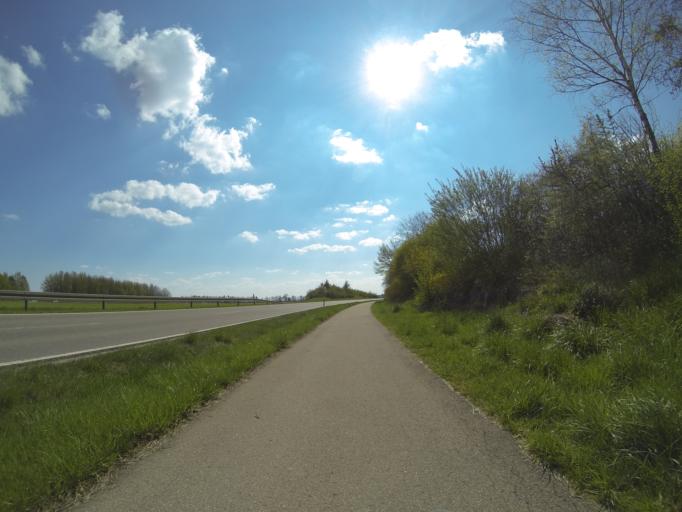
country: DE
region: Baden-Wuerttemberg
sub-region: Tuebingen Region
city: Laupheim
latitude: 48.2235
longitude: 9.8997
